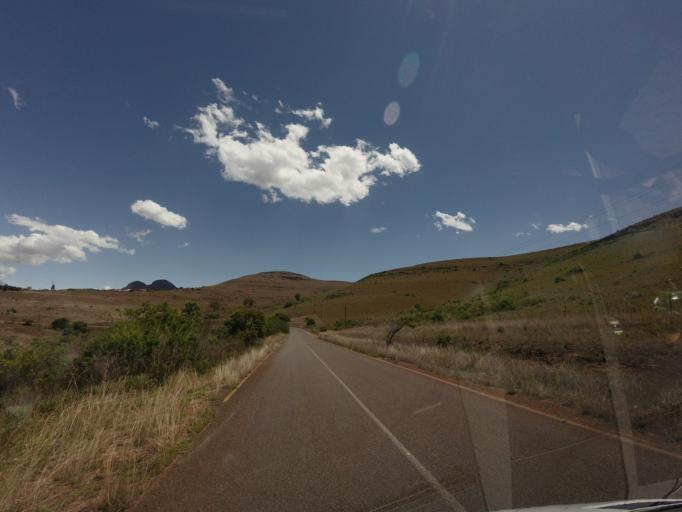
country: ZA
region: Limpopo
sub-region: Mopani District Municipality
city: Hoedspruit
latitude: -24.6046
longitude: 30.7882
